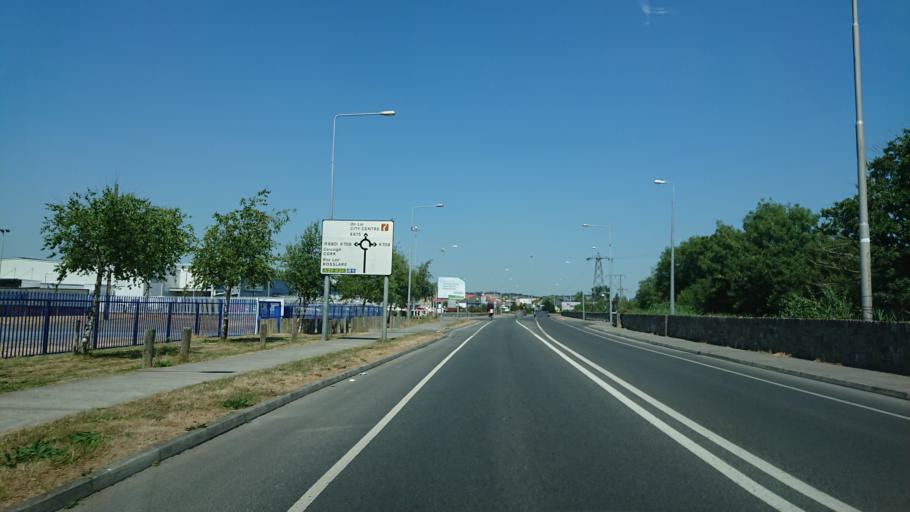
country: IE
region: Munster
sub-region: Waterford
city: Waterford
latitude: 52.2448
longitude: -7.1205
